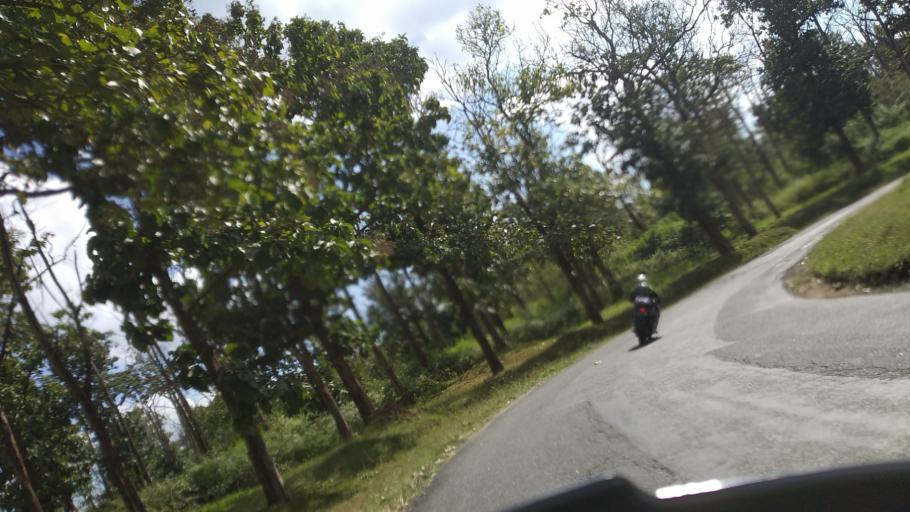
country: IN
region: Kerala
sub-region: Wayanad
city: Panamaram
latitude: 11.9196
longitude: 76.0666
